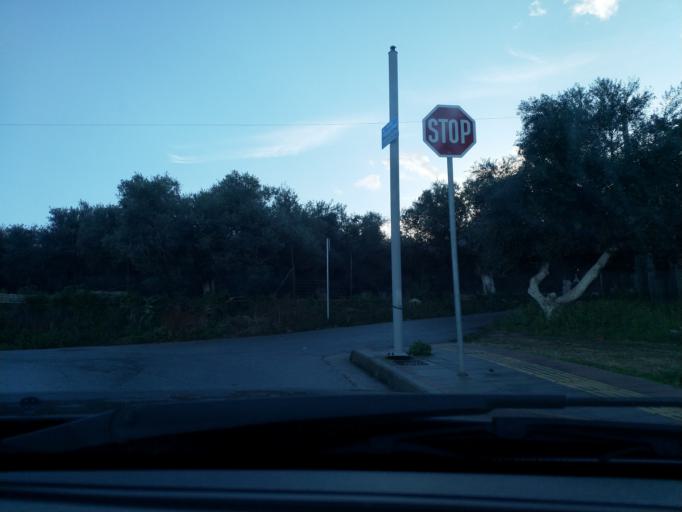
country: GR
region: Crete
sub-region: Nomos Chanias
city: Chania
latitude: 35.5119
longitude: 24.0474
